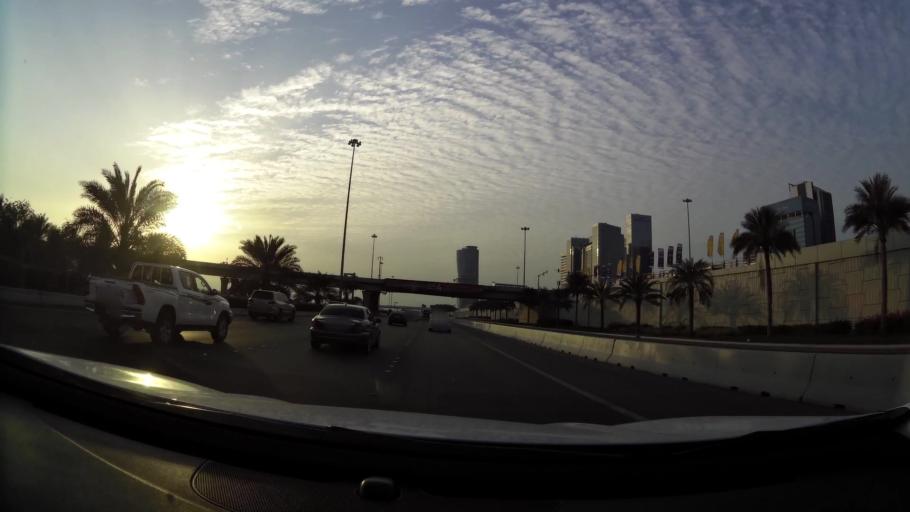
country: AE
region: Abu Dhabi
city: Abu Dhabi
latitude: 24.4152
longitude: 54.4444
